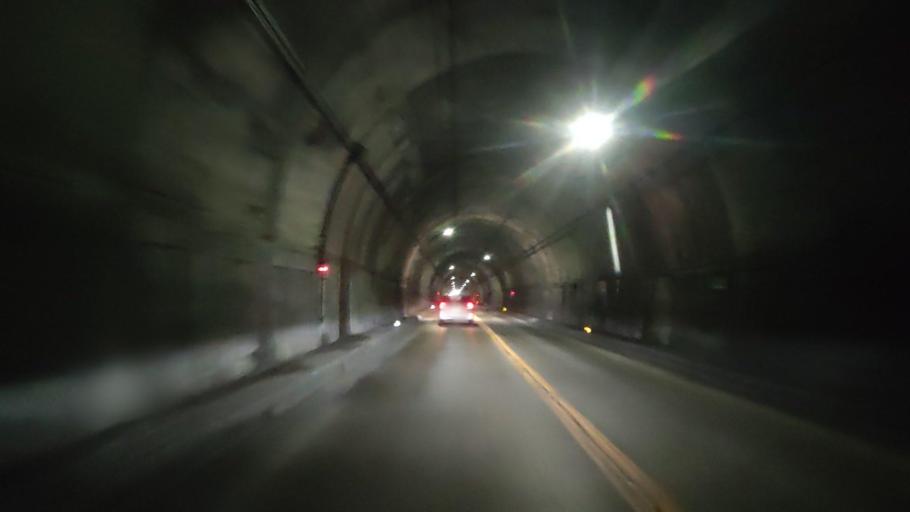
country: JP
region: Nara
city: Yoshino-cho
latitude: 34.3680
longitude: 135.9156
